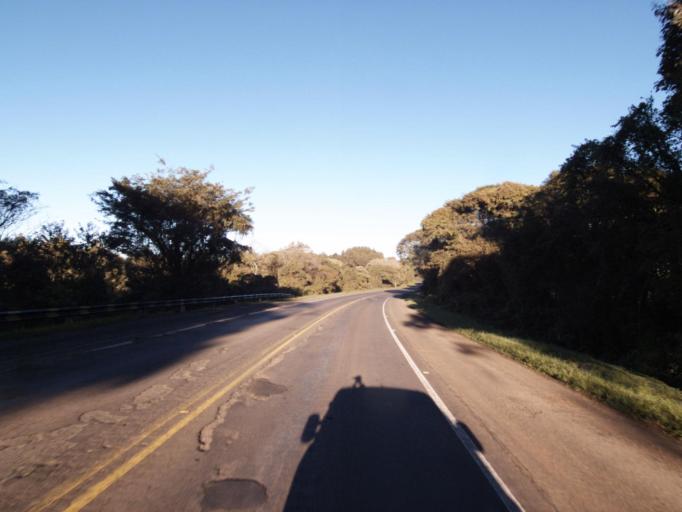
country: BR
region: Santa Catarina
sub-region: Sao Lourenco Do Oeste
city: Sao Lourenco dOeste
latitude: -26.7744
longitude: -53.2719
